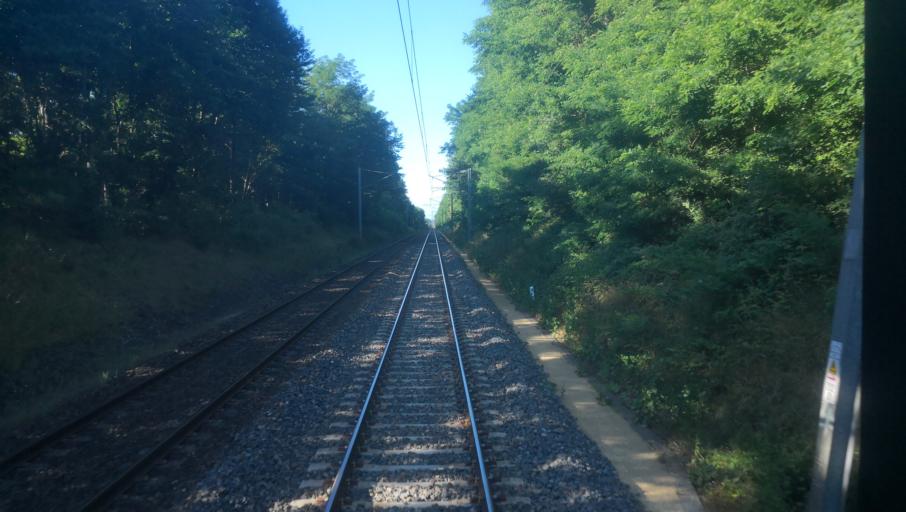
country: FR
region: Centre
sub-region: Departement du Cher
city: Saint-Satur
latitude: 47.3532
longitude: 2.8868
